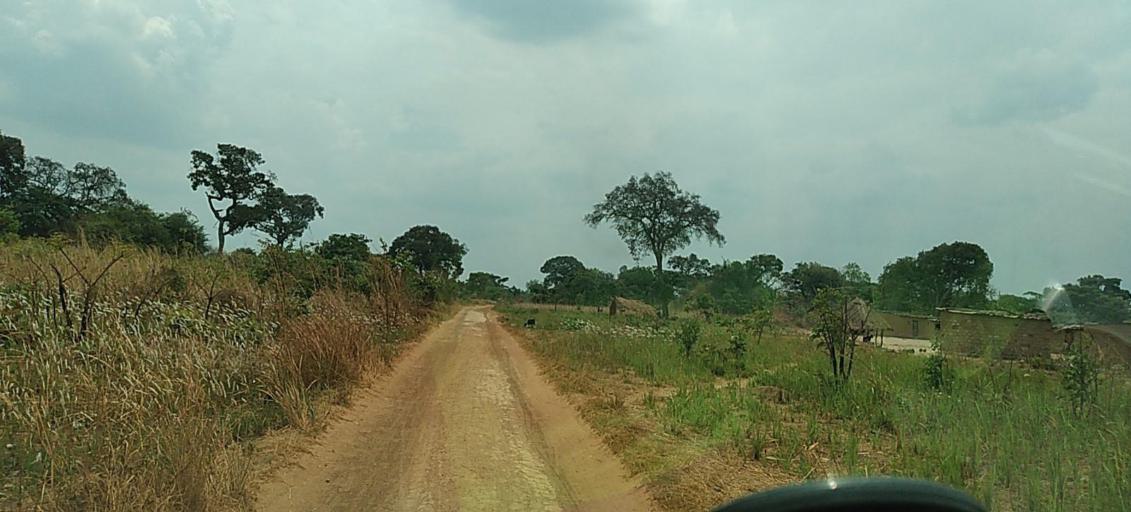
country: ZM
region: North-Western
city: Kansanshi
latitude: -12.0560
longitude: 26.3446
